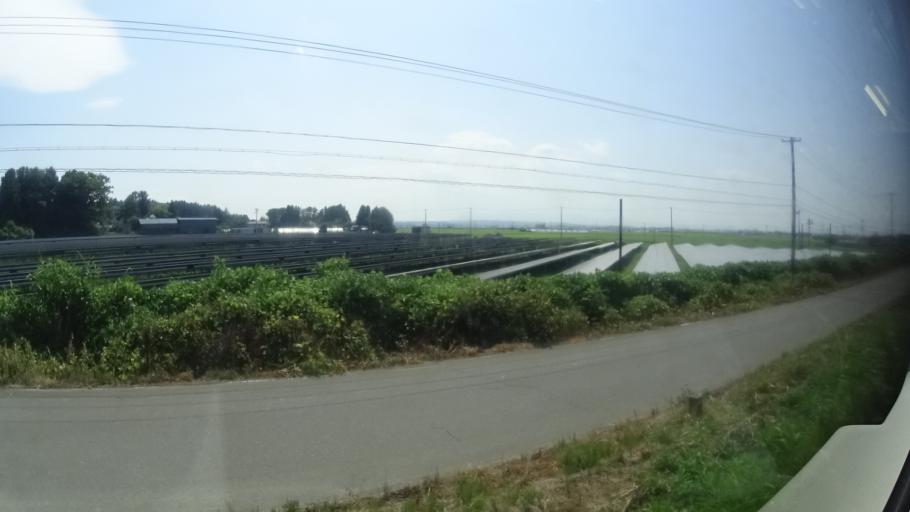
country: JP
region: Miyagi
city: Wakuya
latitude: 38.5271
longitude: 141.1492
